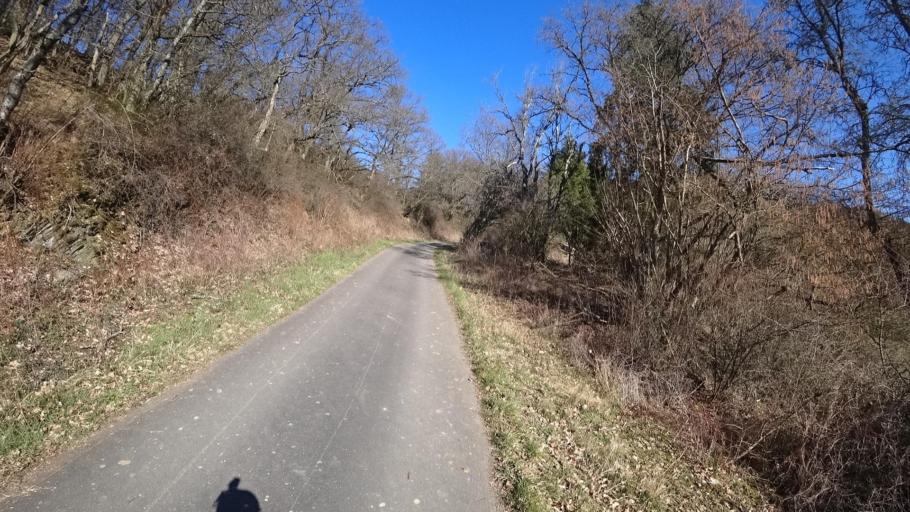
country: DE
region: Rheinland-Pfalz
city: Ravengiersburg
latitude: 49.9363
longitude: 7.4923
